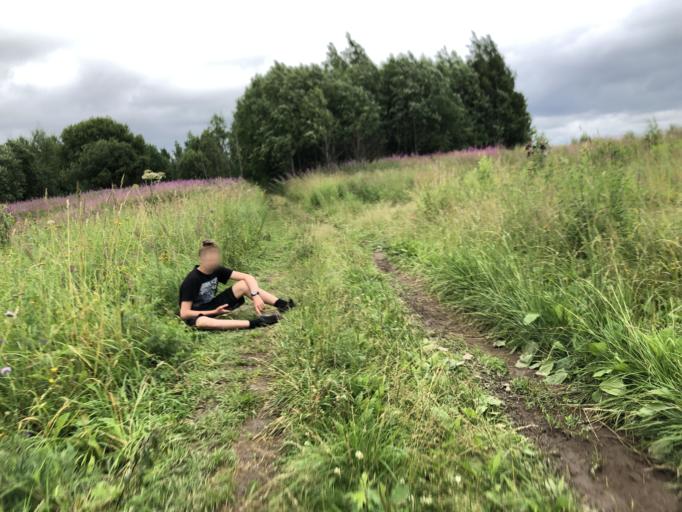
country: RU
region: Tverskaya
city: Rzhev
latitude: 56.2380
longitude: 34.3837
